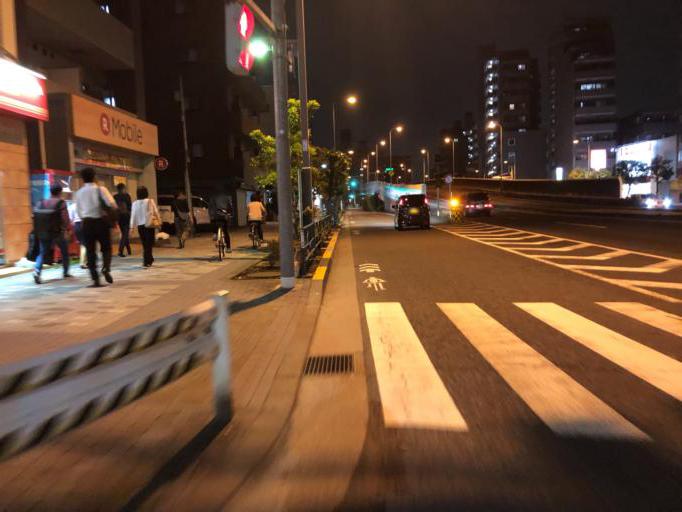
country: JP
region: Tokyo
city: Urayasu
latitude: 35.6655
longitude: 139.8731
